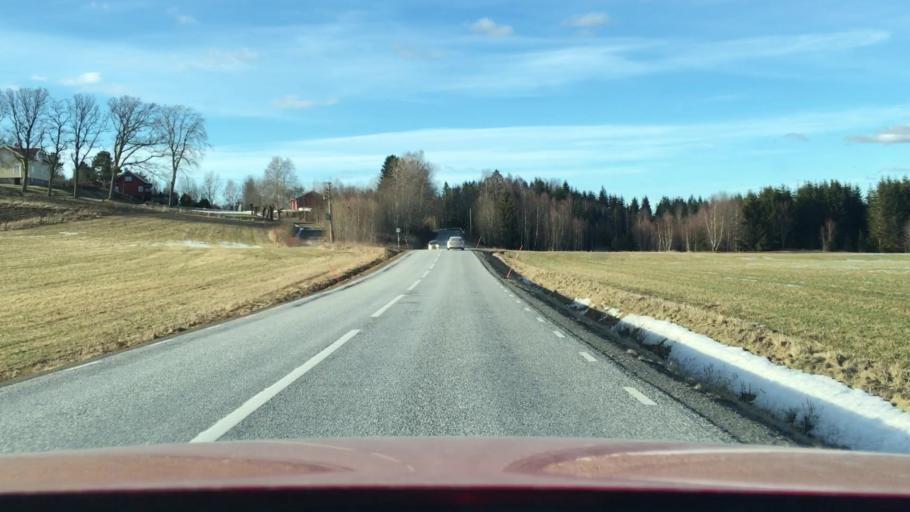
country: SE
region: Vaestra Goetaland
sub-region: Tanums Kommun
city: Tanumshede
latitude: 58.8070
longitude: 11.5528
